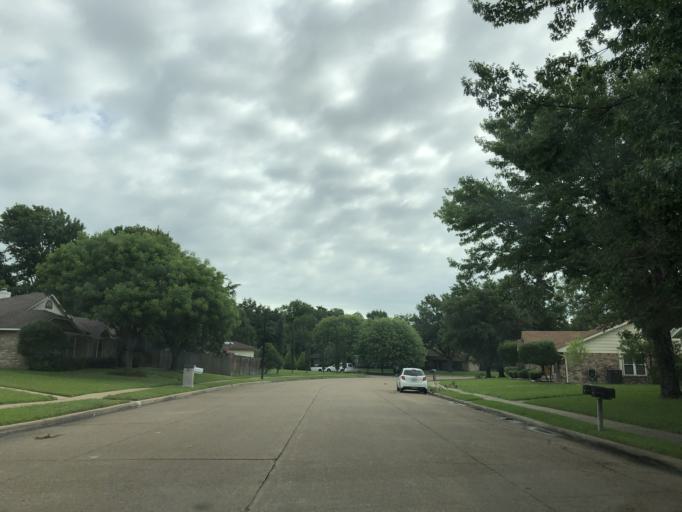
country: US
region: Texas
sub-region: Dallas County
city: Sunnyvale
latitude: 32.8444
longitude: -96.6123
